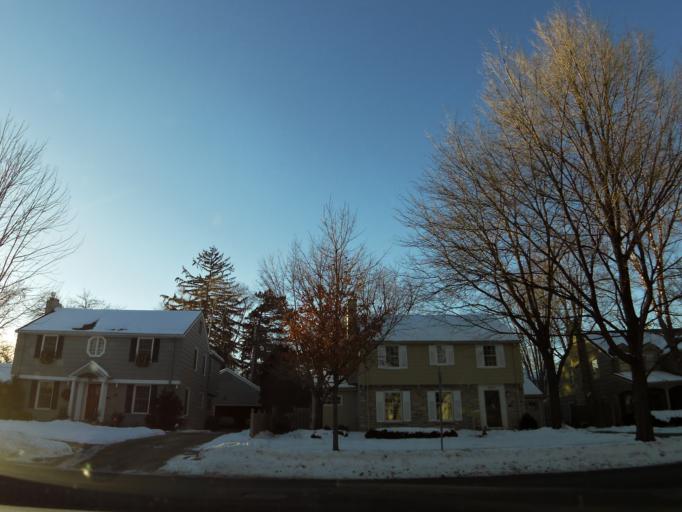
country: US
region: Minnesota
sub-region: Hennepin County
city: Edina
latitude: 44.9143
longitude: -93.3335
